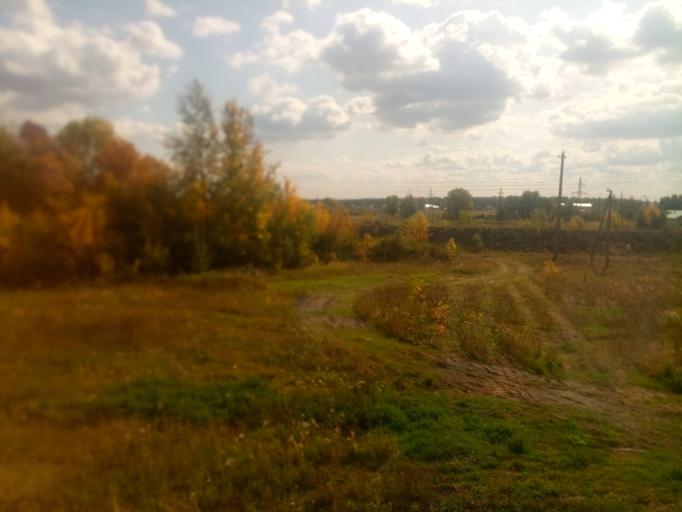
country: RU
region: Chuvashia
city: Urmary
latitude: 55.6913
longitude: 47.9571
